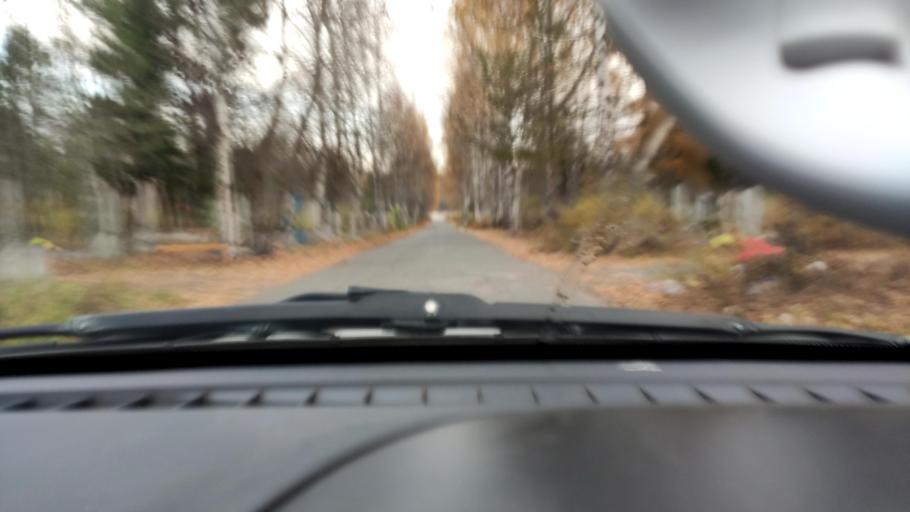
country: RU
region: Perm
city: Kondratovo
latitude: 58.0668
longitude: 56.1351
